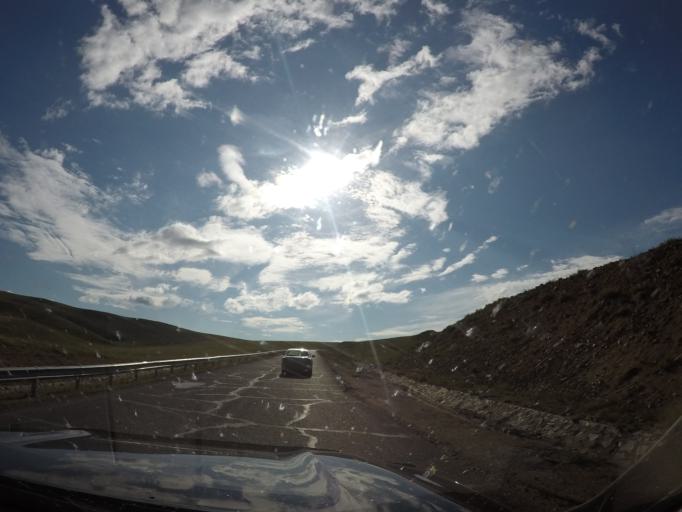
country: MN
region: Hentiy
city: Modot
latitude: 47.7944
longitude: 108.7684
